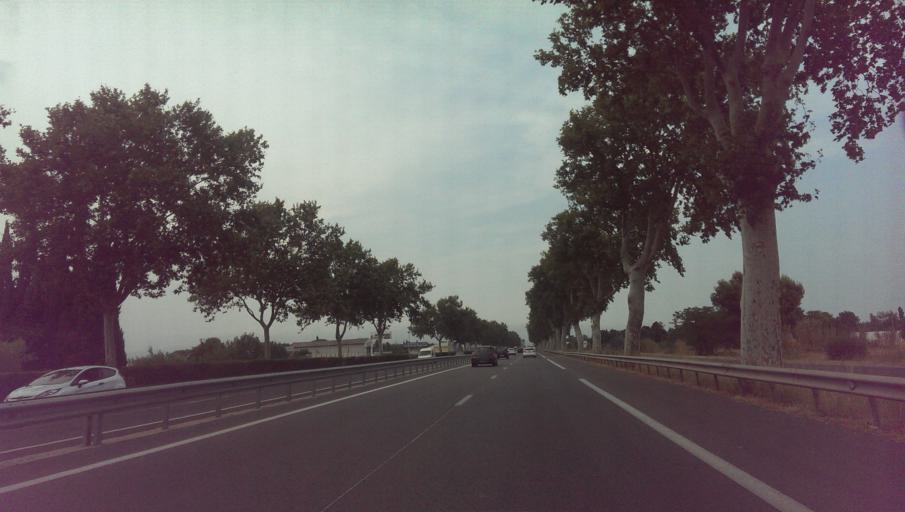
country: FR
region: Languedoc-Roussillon
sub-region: Departement des Pyrenees-Orientales
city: Pia
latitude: 42.7600
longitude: 2.8976
